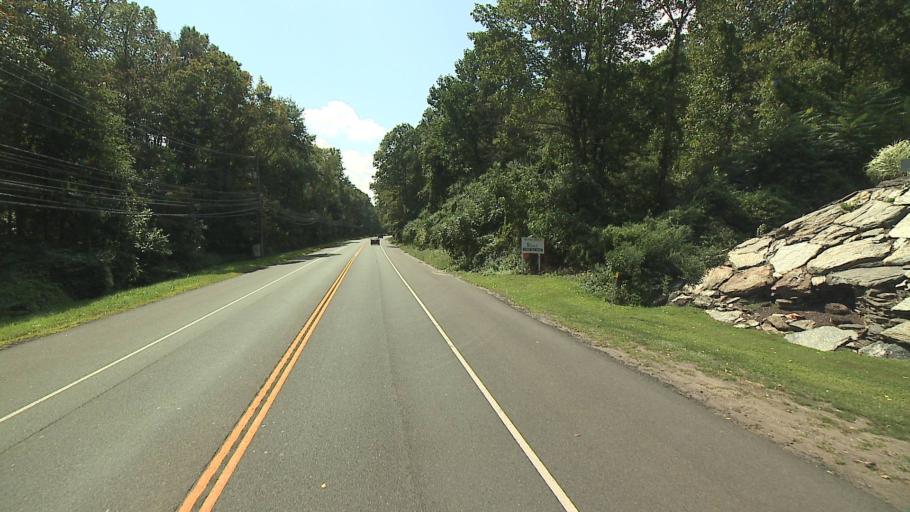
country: US
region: Connecticut
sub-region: Fairfield County
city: Shelton
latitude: 41.2857
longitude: -73.1149
